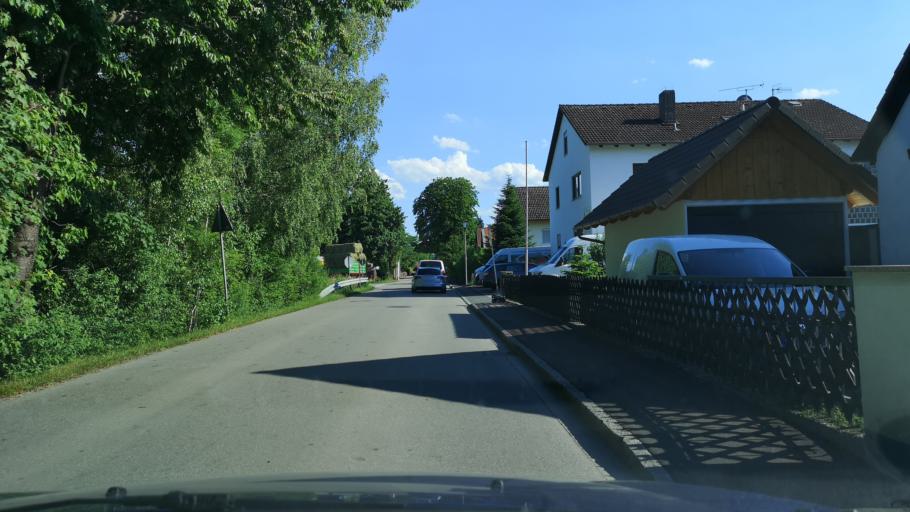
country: DE
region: Bavaria
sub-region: Upper Bavaria
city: Eichenried
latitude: 48.2443
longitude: 11.7807
